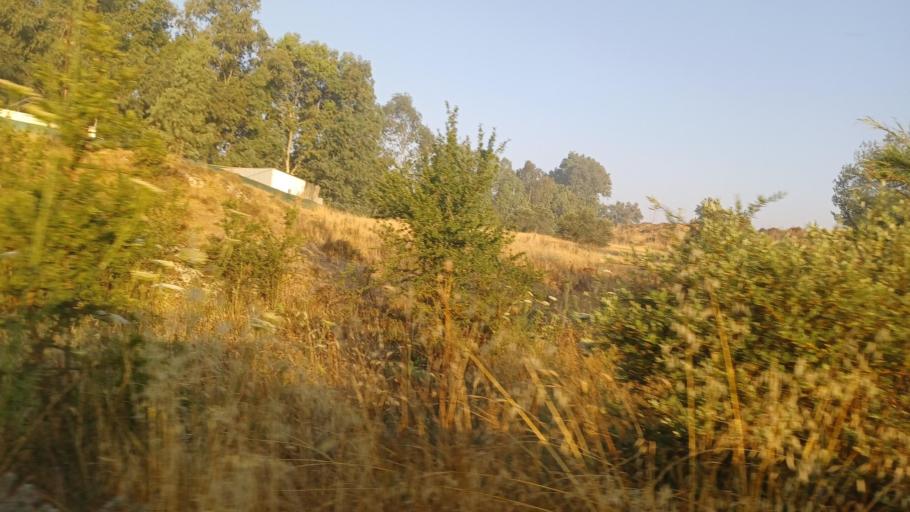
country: CY
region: Lefkosia
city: Alampra
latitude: 34.9764
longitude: 33.4195
